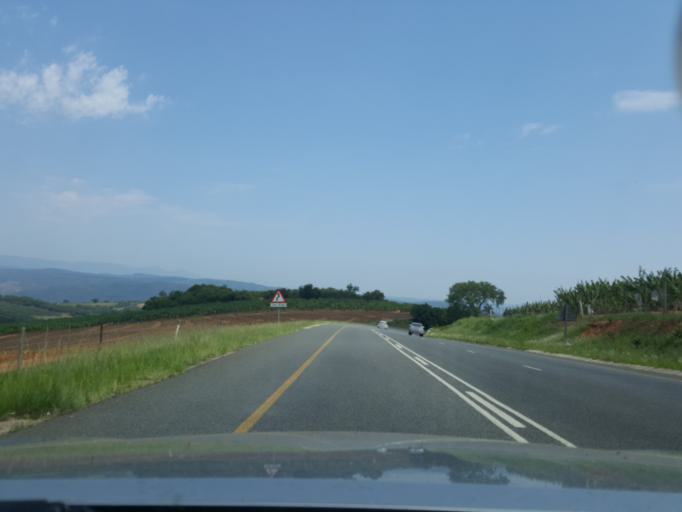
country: ZA
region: Mpumalanga
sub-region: Ehlanzeni District
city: White River
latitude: -25.0755
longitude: 31.1039
